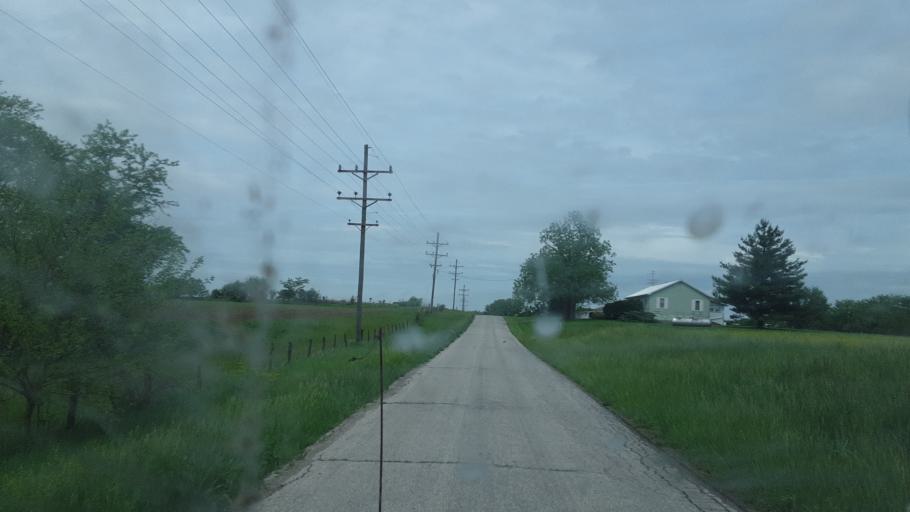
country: US
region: Missouri
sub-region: Clark County
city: Kahoka
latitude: 40.4238
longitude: -91.5957
